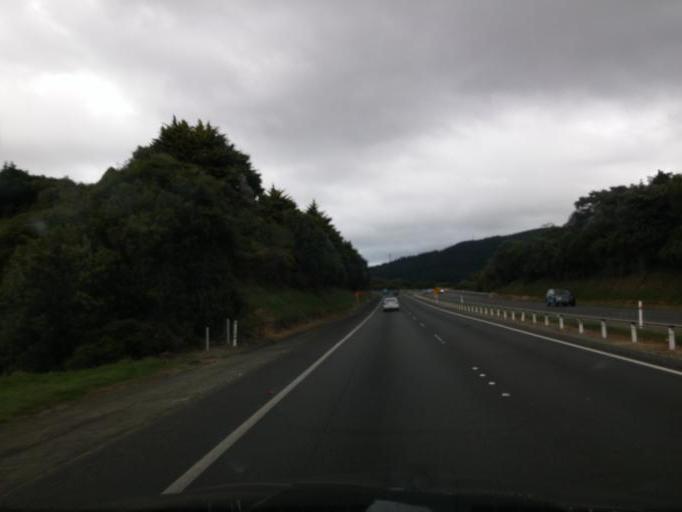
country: NZ
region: Wellington
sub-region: Porirua City
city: Porirua
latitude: -41.1776
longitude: 174.8298
